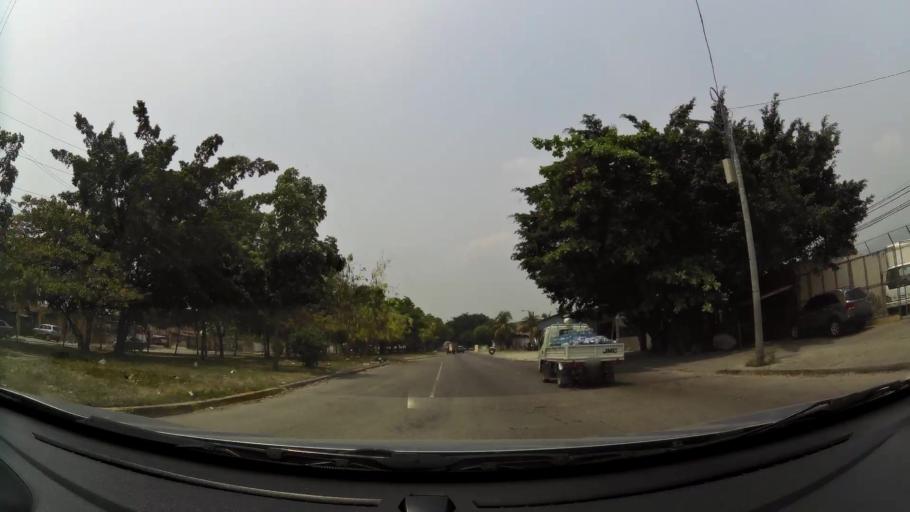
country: HN
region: Cortes
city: San Pedro Sula
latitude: 15.4926
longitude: -88.0058
